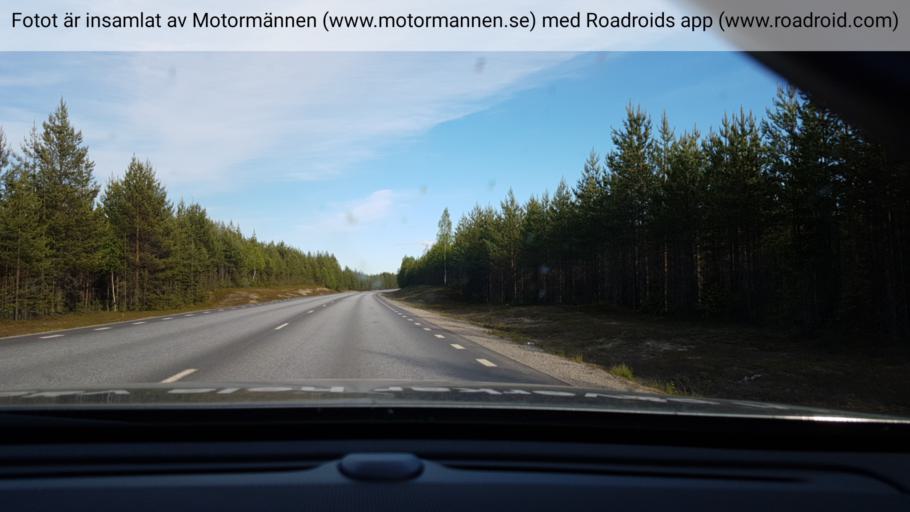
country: SE
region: Vaesterbotten
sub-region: Vindelns Kommun
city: Vindeln
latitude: 64.1579
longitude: 19.8386
